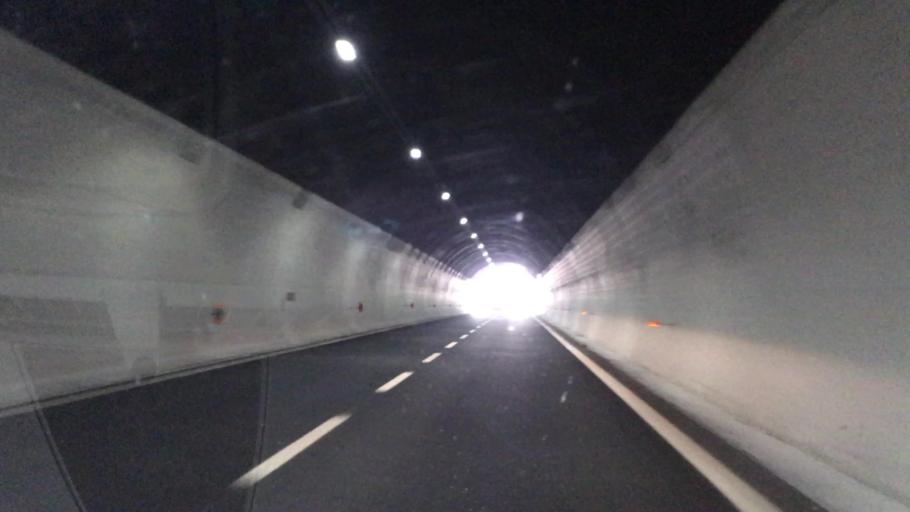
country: IT
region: Liguria
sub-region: Provincia di Genova
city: Sestri Levante
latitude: 44.2874
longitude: 9.3928
